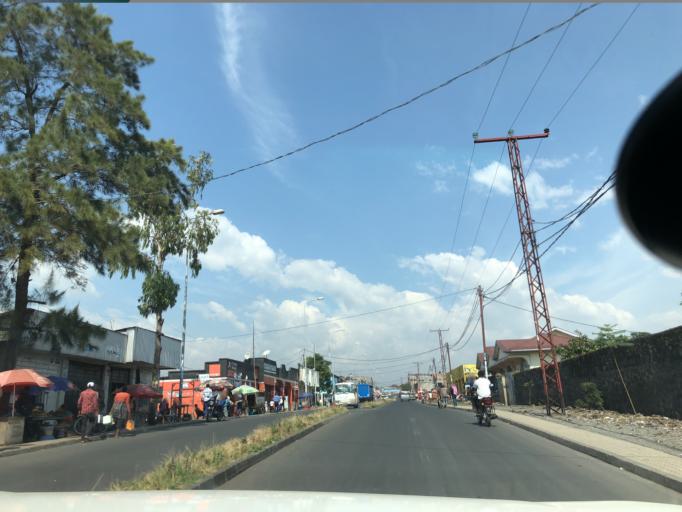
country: CD
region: Nord Kivu
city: Goma
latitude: -1.6575
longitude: 29.1935
